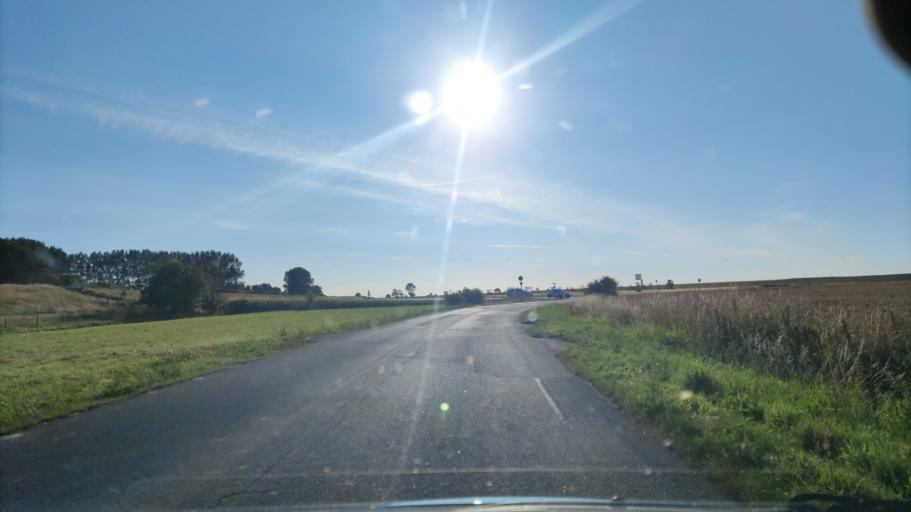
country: DE
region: Lower Saxony
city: Werdum
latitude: 53.6996
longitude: 7.8037
